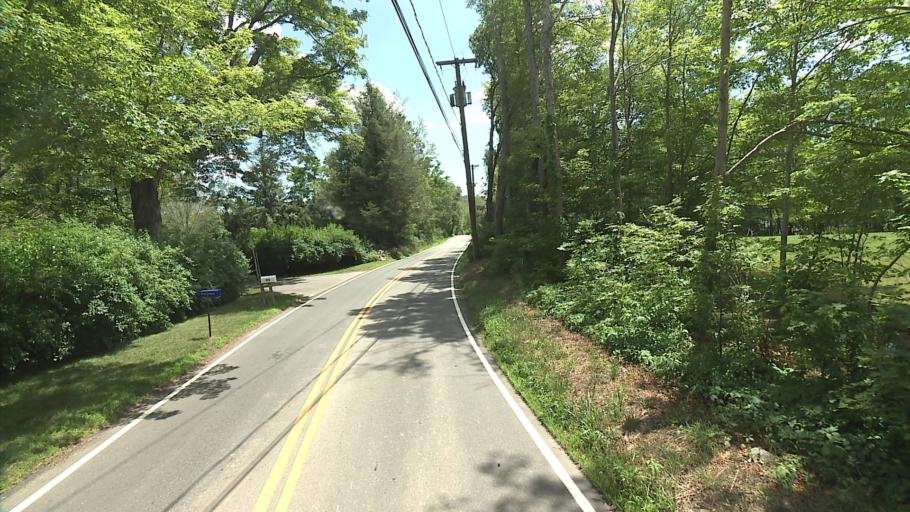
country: US
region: Connecticut
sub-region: New London County
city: Colchester
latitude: 41.4935
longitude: -72.3474
